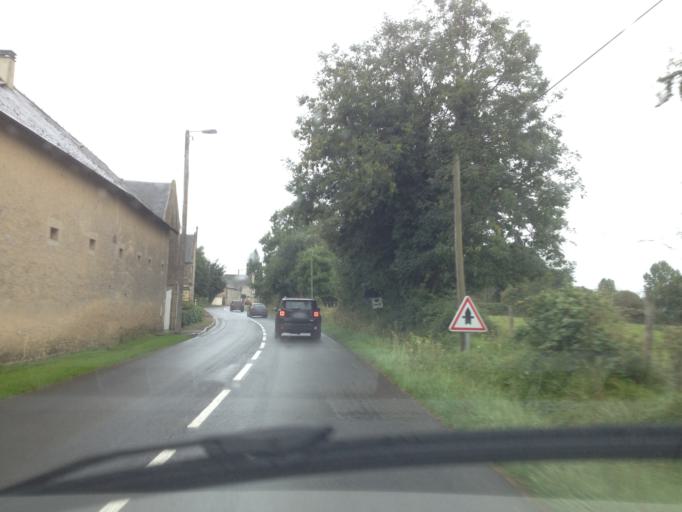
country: FR
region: Lower Normandy
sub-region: Departement du Calvados
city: Saint-Vigor-le-Grand
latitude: 49.3043
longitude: -0.6808
